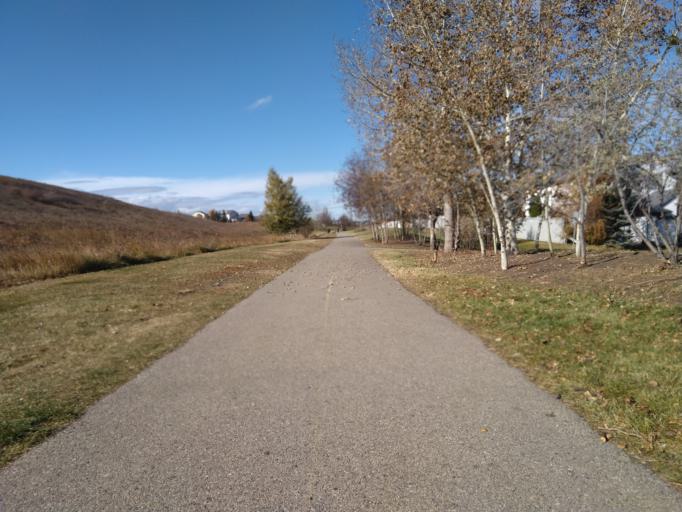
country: CA
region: Alberta
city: Calgary
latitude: 51.1482
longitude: -114.1069
